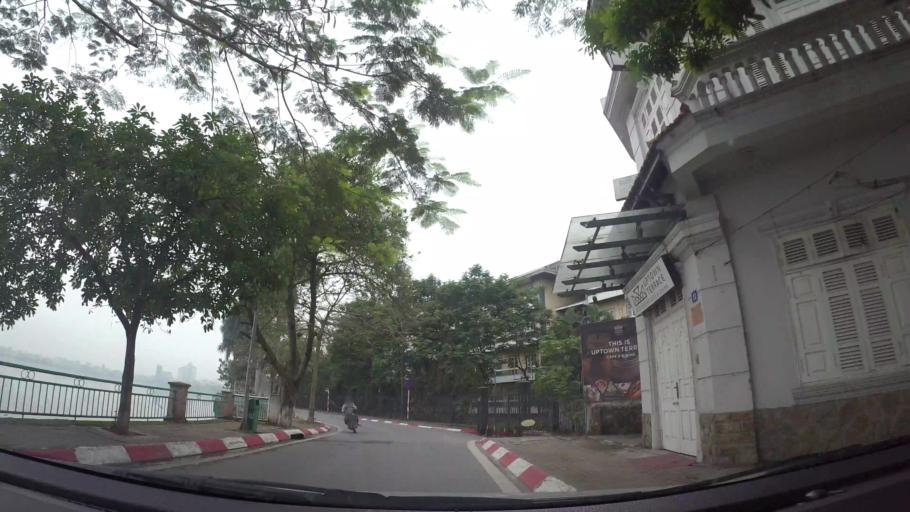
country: VN
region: Ha Noi
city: Dong Da
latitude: 21.0420
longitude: 105.8267
